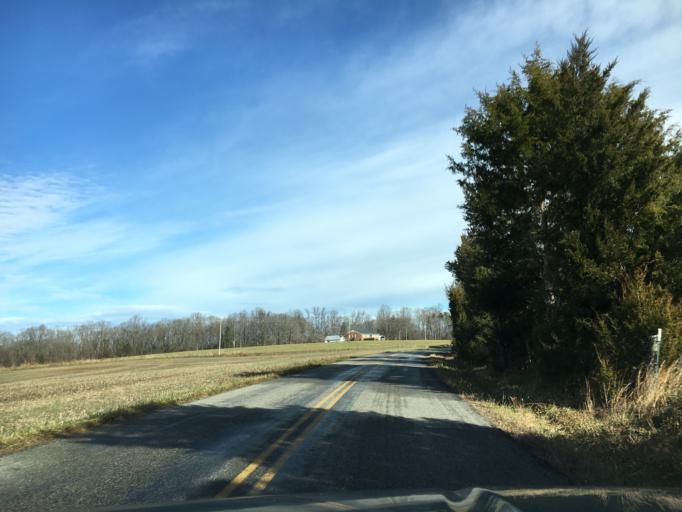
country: US
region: Virginia
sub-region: Nottoway County
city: Crewe
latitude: 37.3216
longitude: -78.1741
